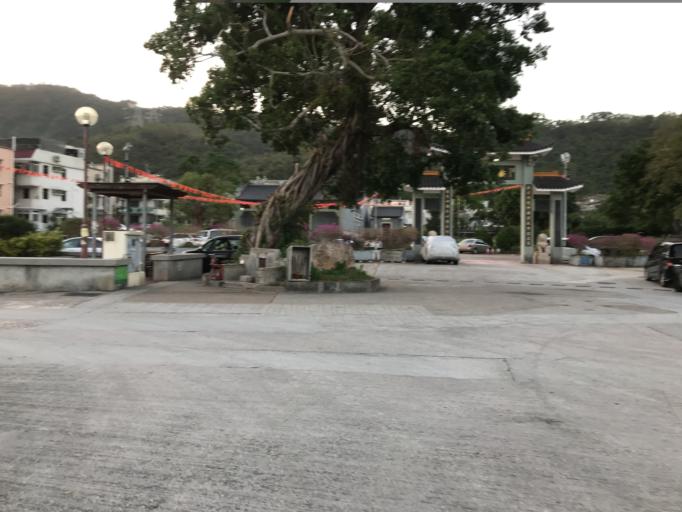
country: HK
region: Tai Po
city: Tai Po
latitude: 22.4694
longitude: 114.1493
